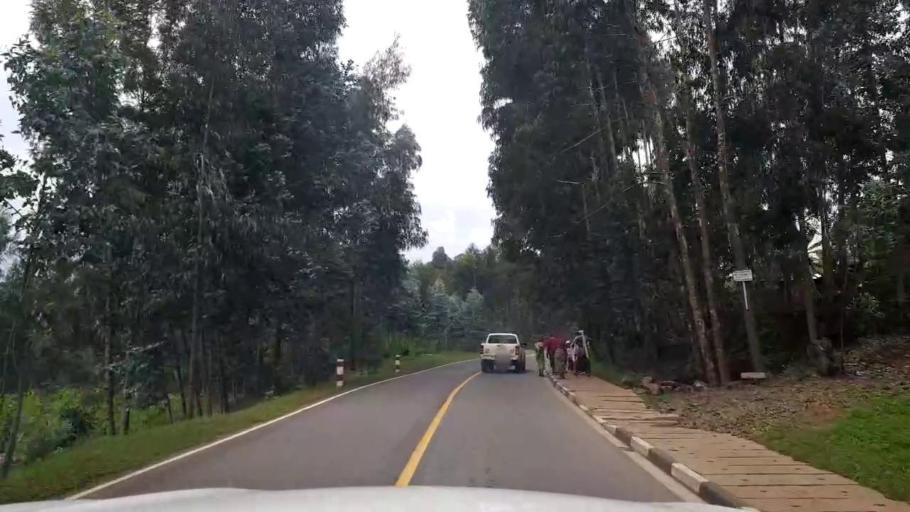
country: RW
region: Northern Province
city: Musanze
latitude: -1.4530
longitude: 29.6074
